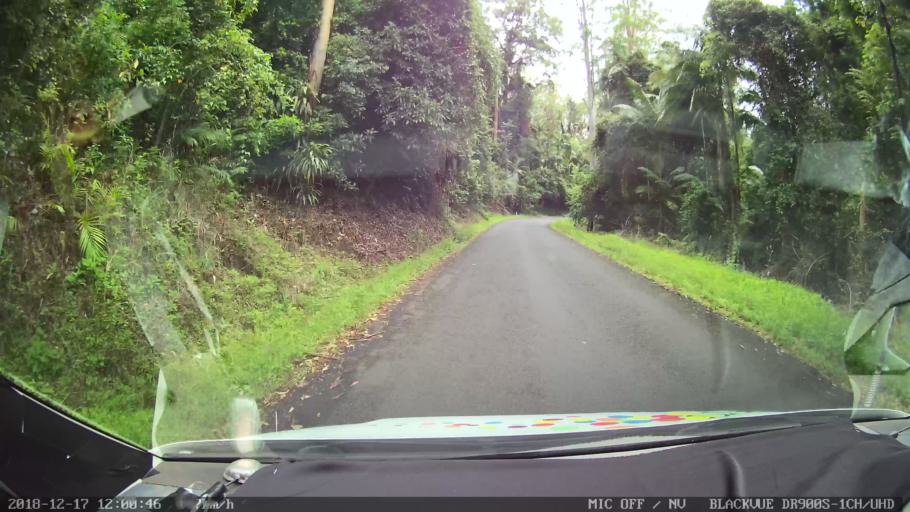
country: AU
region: New South Wales
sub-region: Kyogle
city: Kyogle
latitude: -28.5238
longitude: 152.5697
